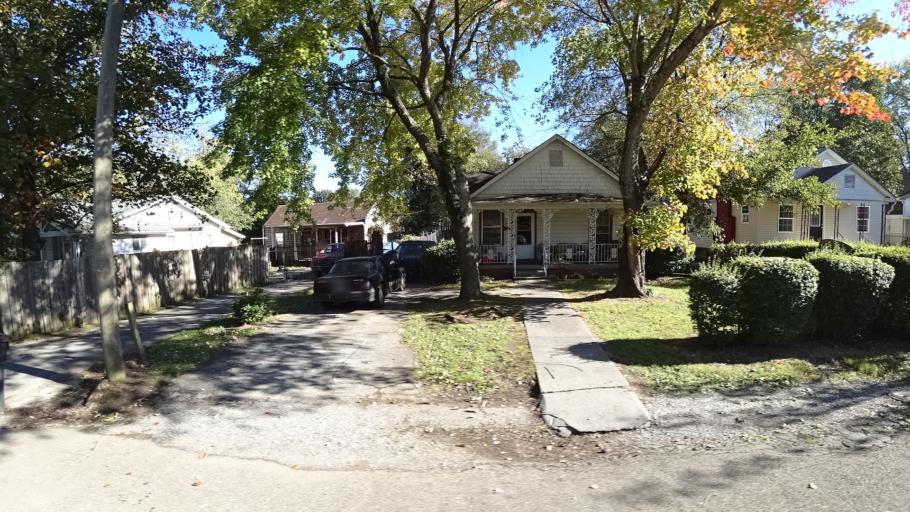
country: US
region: Tennessee
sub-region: Knox County
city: Knoxville
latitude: 35.9831
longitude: -83.8918
